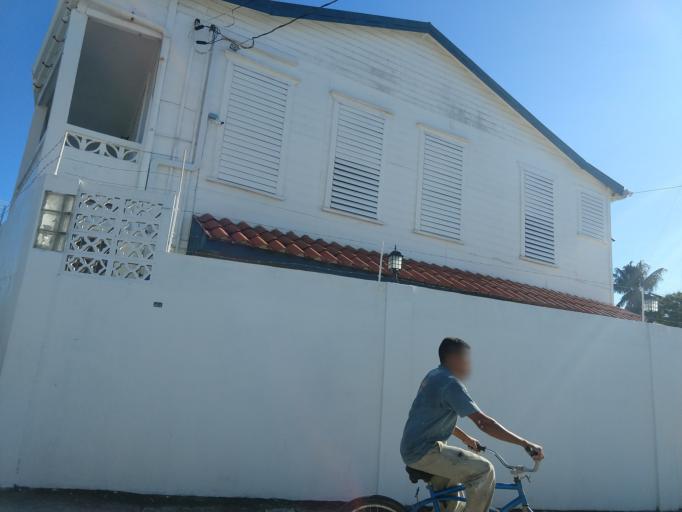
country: BZ
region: Belize
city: Belize City
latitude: 17.4996
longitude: -88.1847
